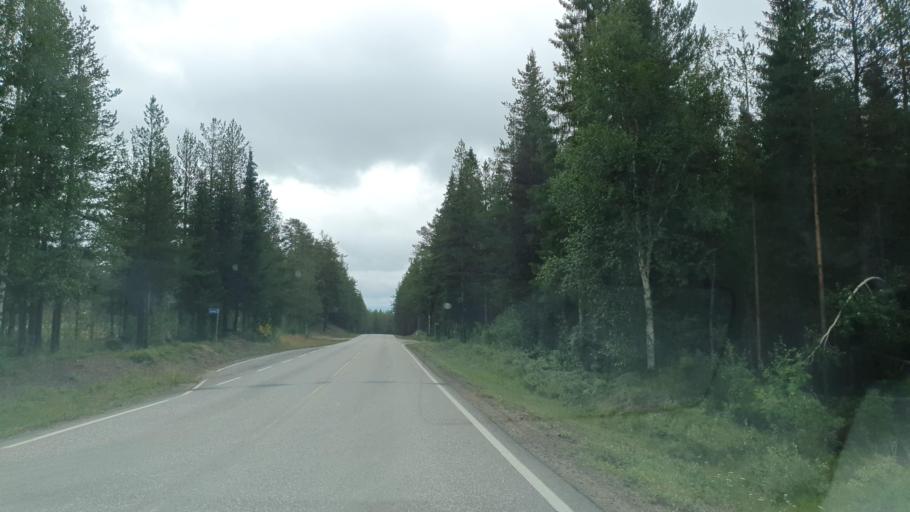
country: FI
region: Lapland
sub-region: Tunturi-Lappi
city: Kolari
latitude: 67.5487
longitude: 23.9828
